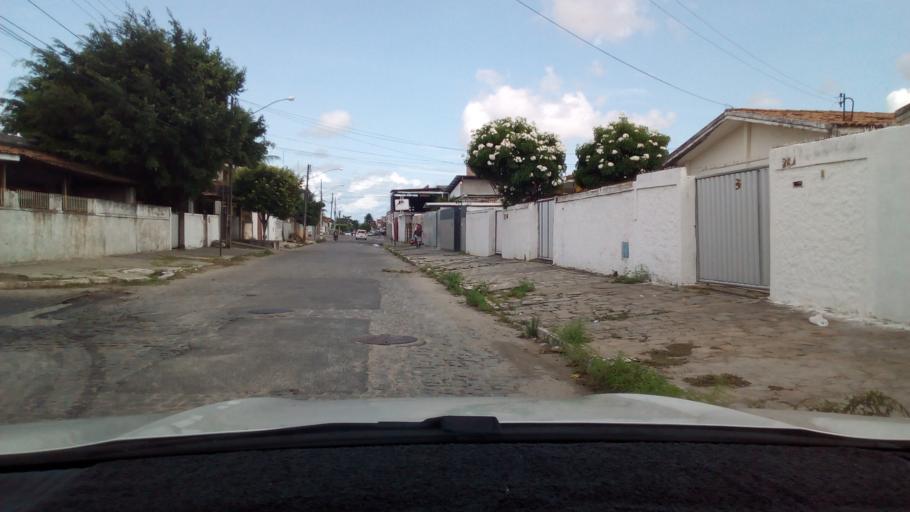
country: BR
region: Paraiba
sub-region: Joao Pessoa
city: Joao Pessoa
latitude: -7.1541
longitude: -34.8729
